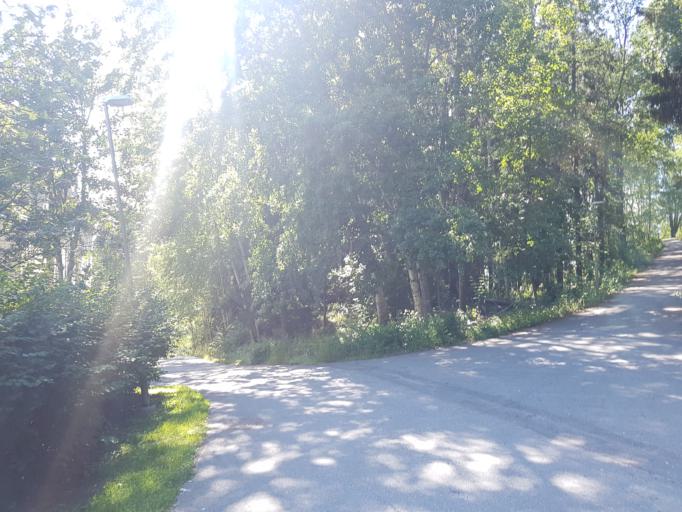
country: SE
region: Stockholm
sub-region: Huddinge Kommun
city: Huddinge
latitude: 59.2146
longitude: 17.9465
